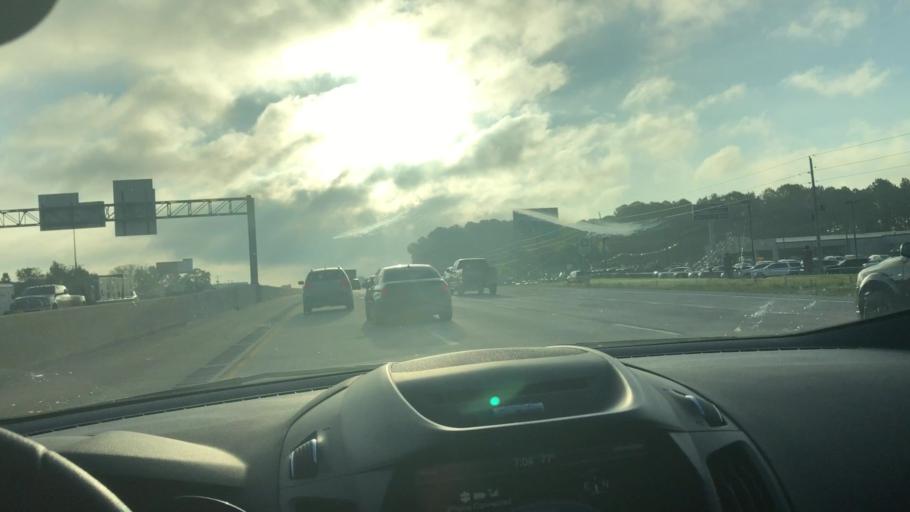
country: US
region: Arkansas
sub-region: Pulaski County
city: Alexander
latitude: 34.6338
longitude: -92.4621
